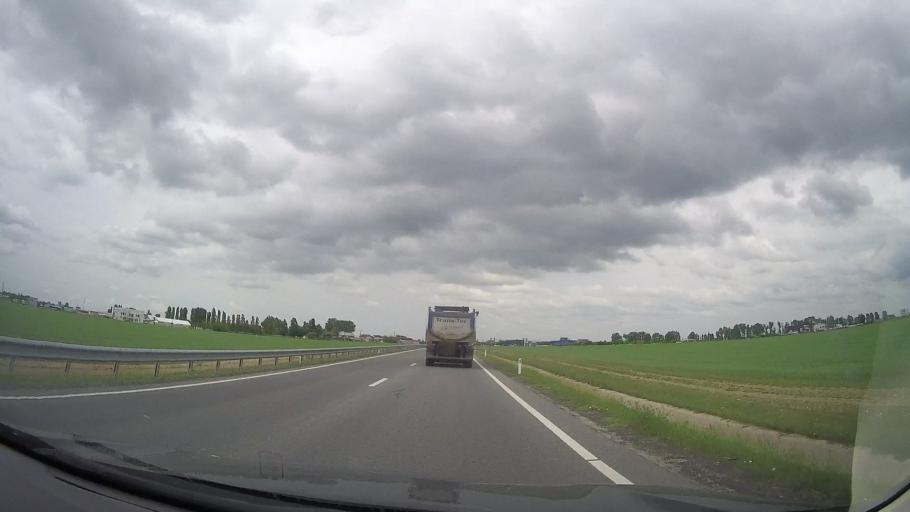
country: RO
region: Dolj
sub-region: Comuna Carcea
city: Carcea
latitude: 44.3101
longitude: 23.9125
